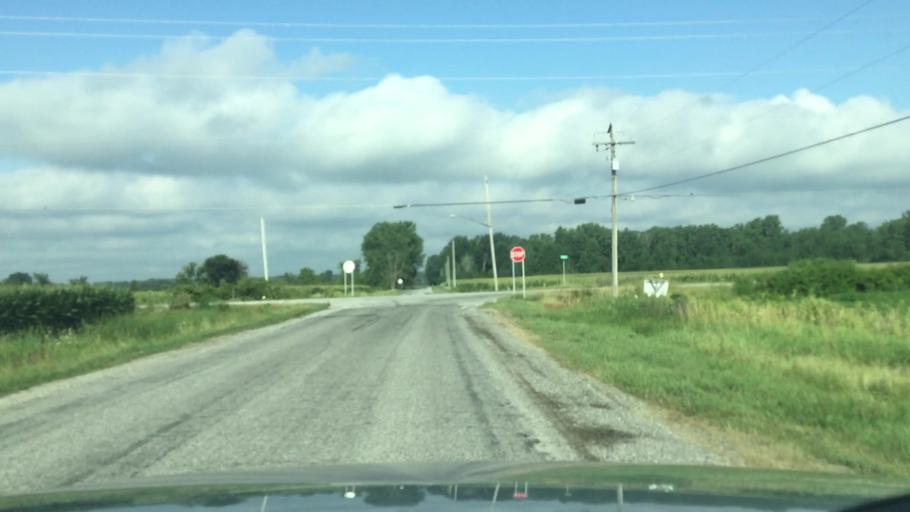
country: US
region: Michigan
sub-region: Saginaw County
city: Frankenmuth
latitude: 43.2789
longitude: -83.7349
